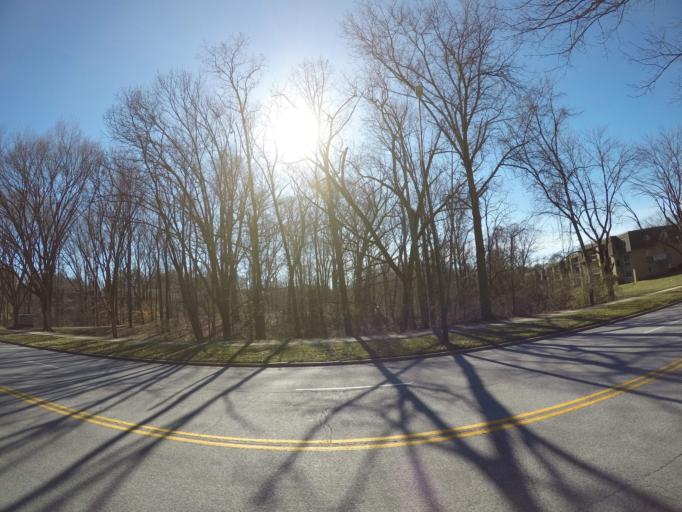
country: US
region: Maryland
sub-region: Howard County
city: Columbia
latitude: 39.2125
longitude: -76.8175
